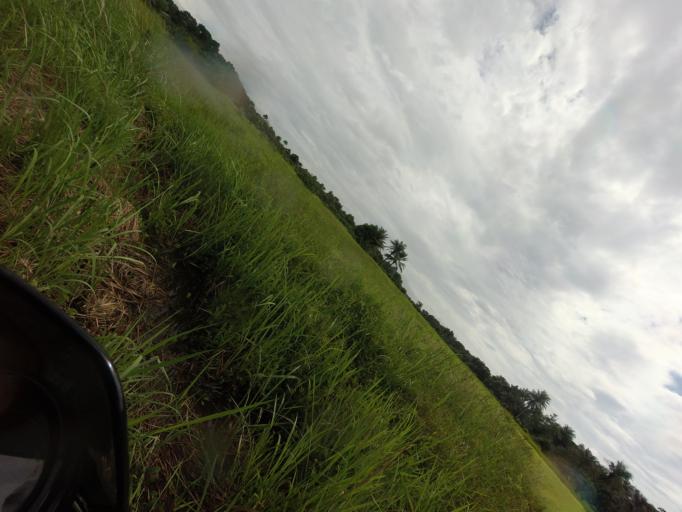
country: SL
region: Northern Province
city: Mambolo
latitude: 9.0020
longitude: -12.9645
